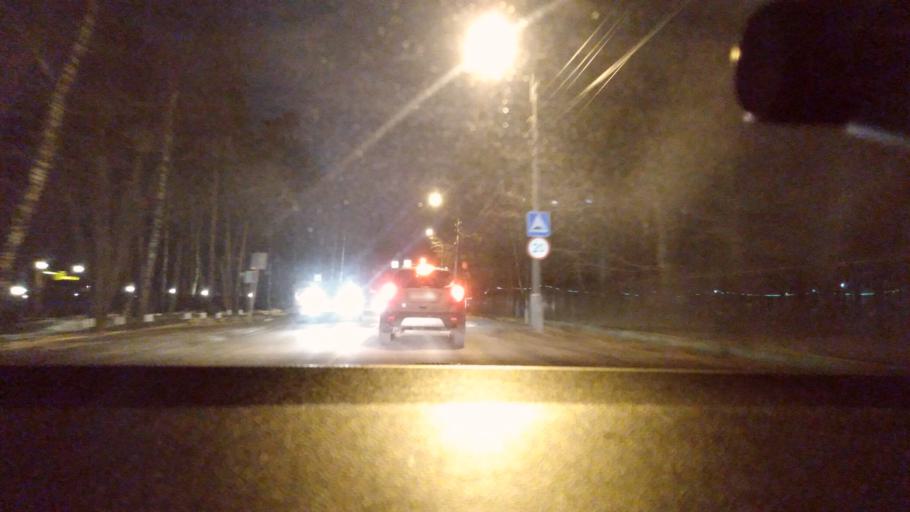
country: RU
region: Moskovskaya
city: Saltykovka
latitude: 55.7815
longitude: 37.9316
